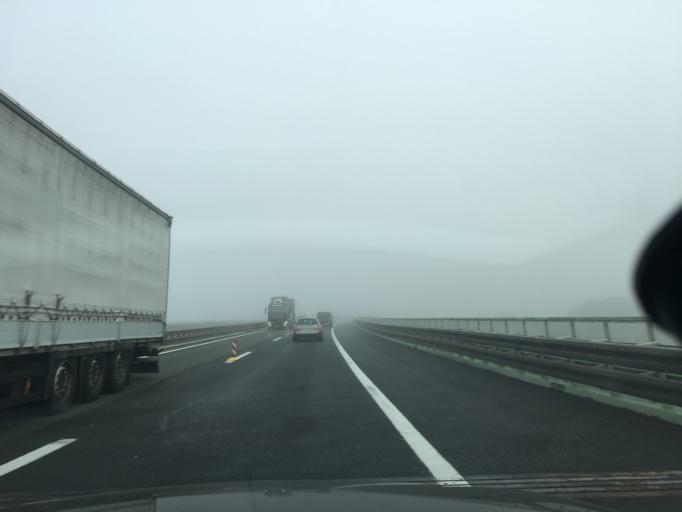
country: HR
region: Licko-Senjska
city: Otocac
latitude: 44.8625
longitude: 15.2108
